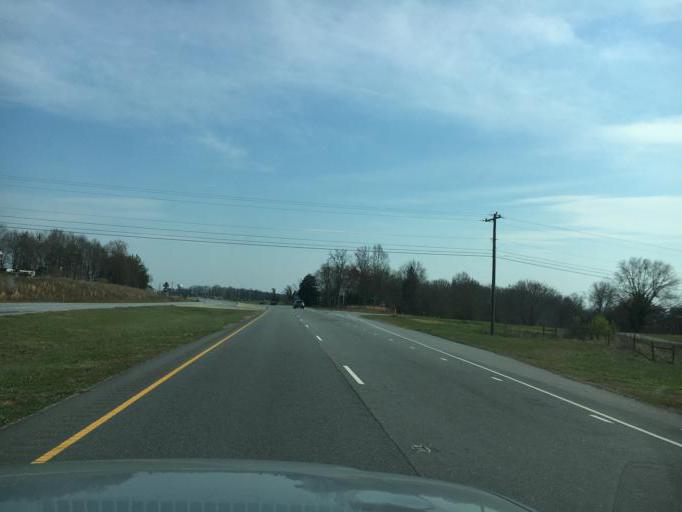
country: US
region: North Carolina
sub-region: Rutherford County
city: Forest City
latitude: 35.2739
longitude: -81.8941
